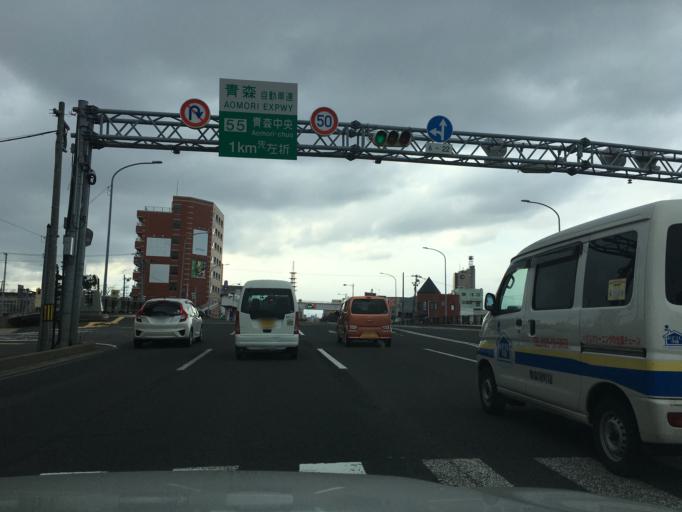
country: JP
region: Aomori
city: Aomori Shi
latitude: 40.8244
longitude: 140.7629
